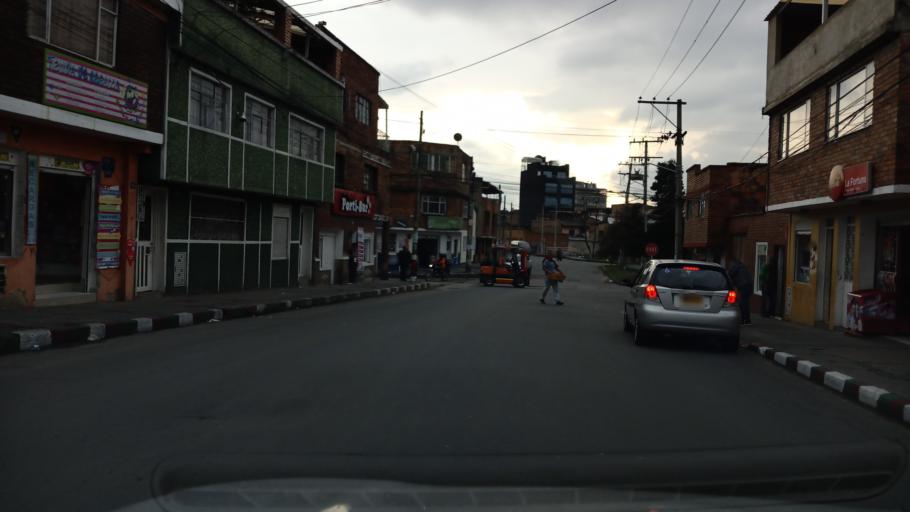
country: CO
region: Bogota D.C.
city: Bogota
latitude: 4.5867
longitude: -74.1139
